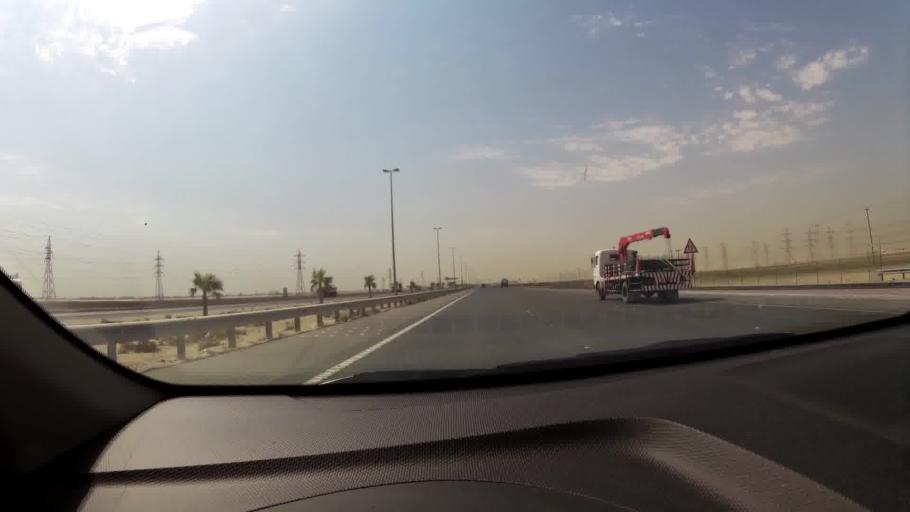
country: KW
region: Al Ahmadi
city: Al Fahahil
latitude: 28.8225
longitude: 48.2587
